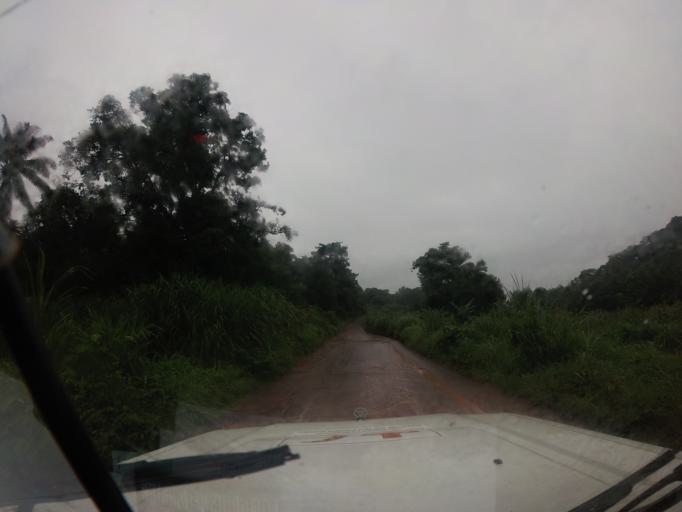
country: SL
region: Northern Province
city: Kabala
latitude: 9.6228
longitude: -11.5509
